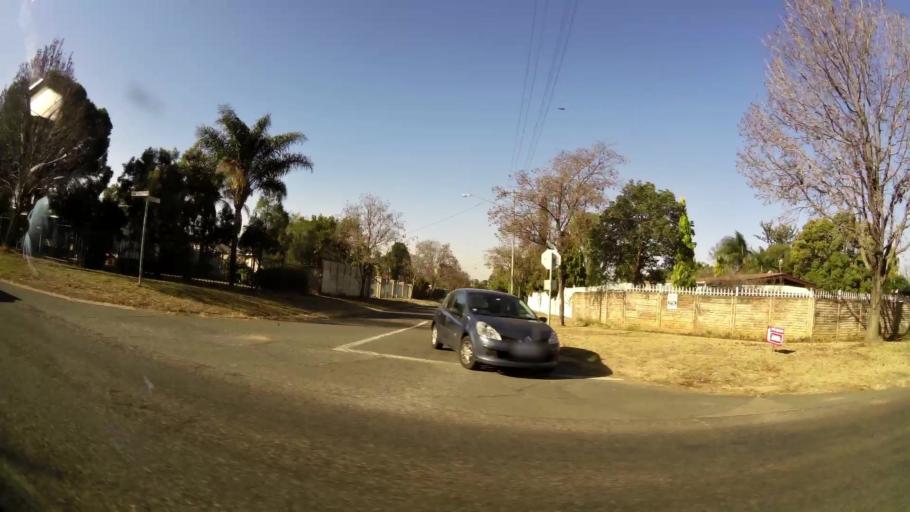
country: ZA
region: Gauteng
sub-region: City of Tshwane Metropolitan Municipality
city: Pretoria
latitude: -25.7136
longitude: 28.2618
